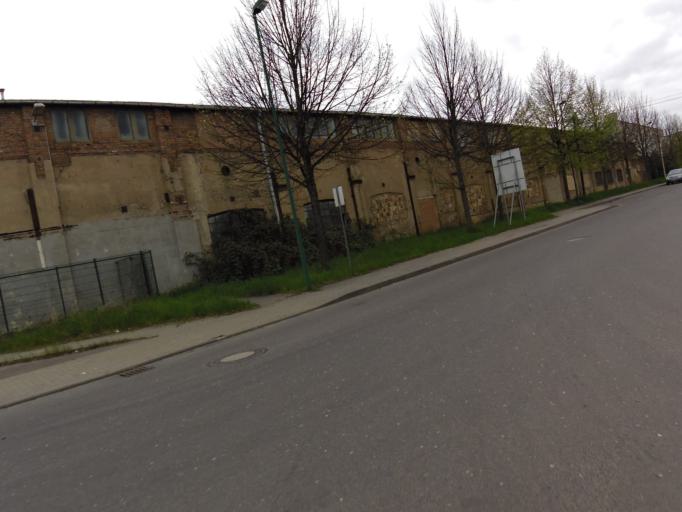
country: DE
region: Saxony
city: Markkleeberg
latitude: 51.2969
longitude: 12.3160
